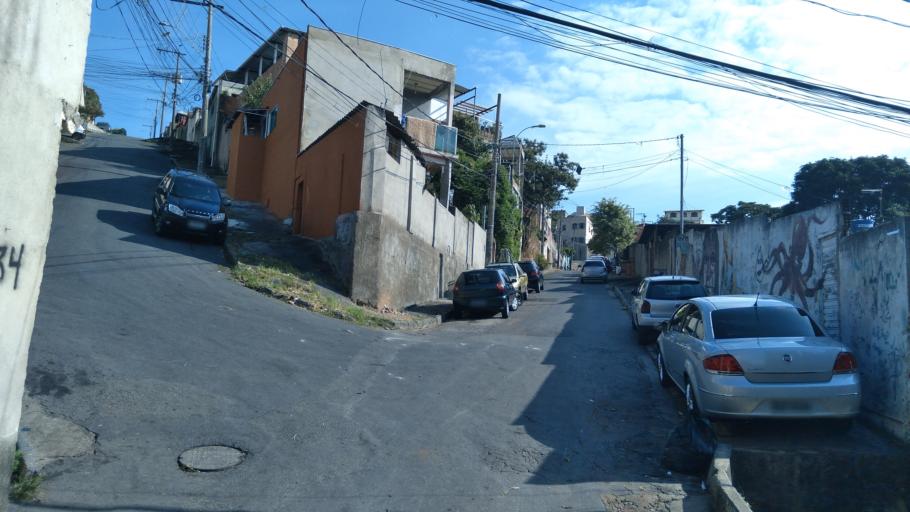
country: BR
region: Minas Gerais
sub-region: Belo Horizonte
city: Belo Horizonte
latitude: -19.8976
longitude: -43.9419
